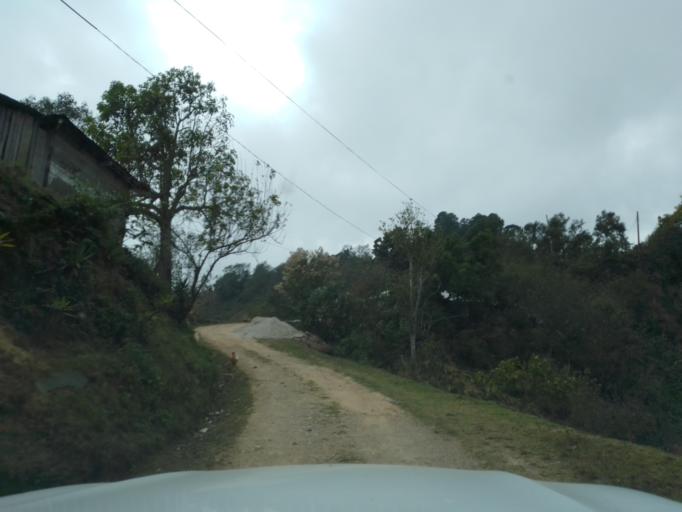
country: GT
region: San Marcos
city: Tacana
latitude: 15.2195
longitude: -92.2108
